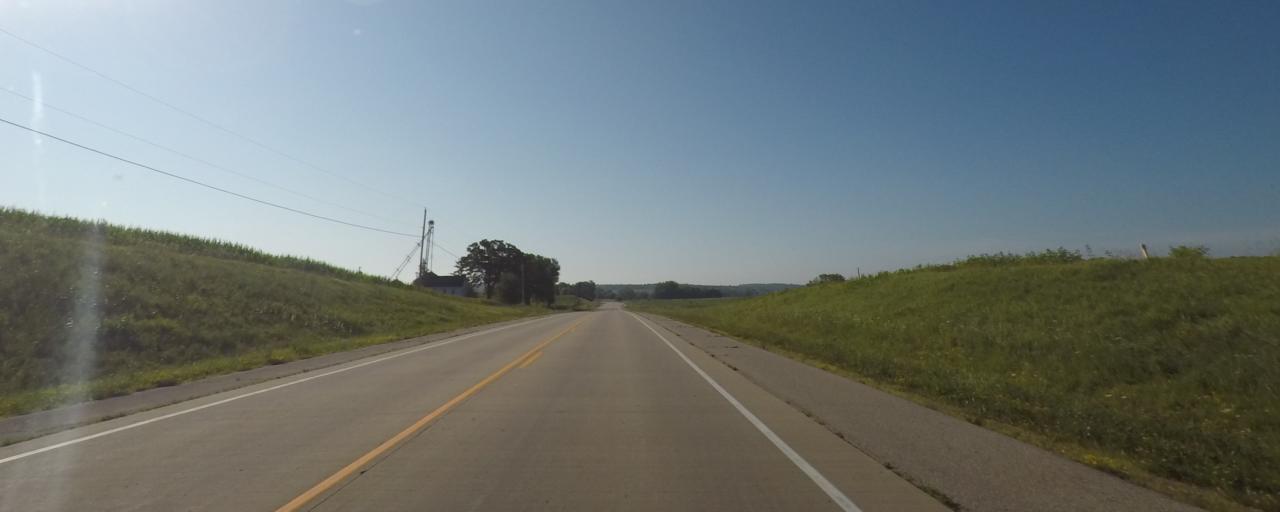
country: US
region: Wisconsin
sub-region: Jefferson County
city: Lake Ripley
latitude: 42.9832
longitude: -88.9688
